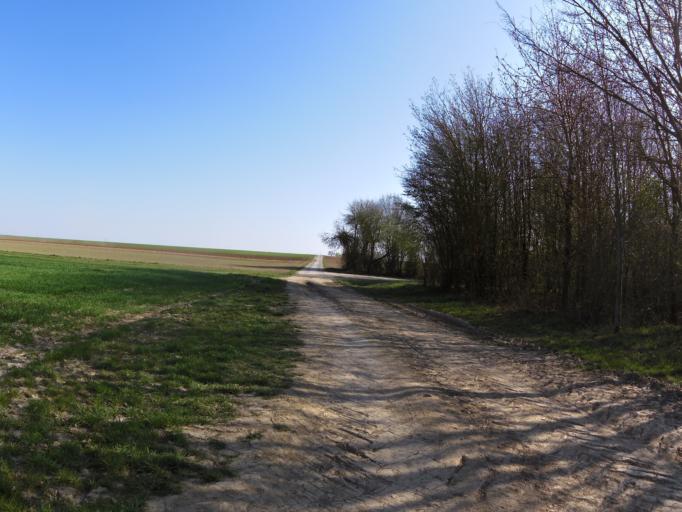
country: DE
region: Bavaria
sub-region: Regierungsbezirk Unterfranken
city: Oberpleichfeld
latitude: 49.8324
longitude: 10.0897
